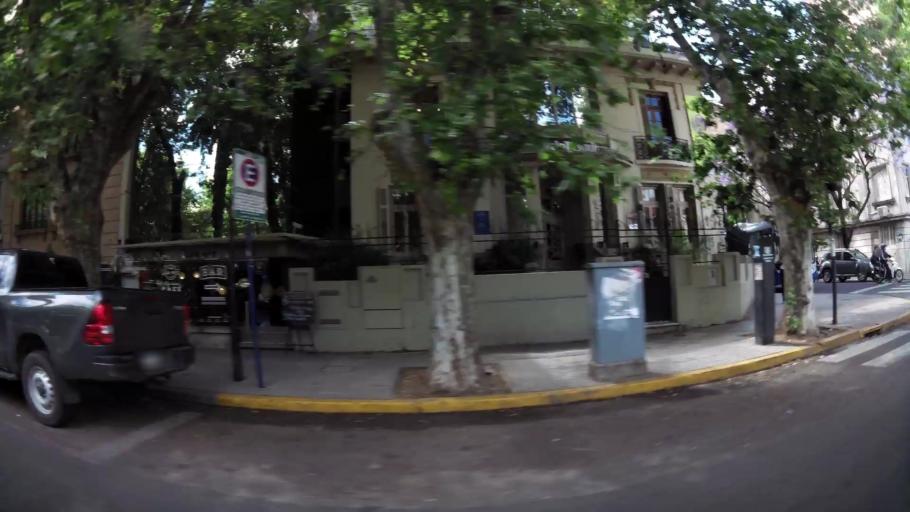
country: AR
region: Santa Fe
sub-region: Departamento de Rosario
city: Rosario
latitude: -32.9402
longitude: -60.6522
